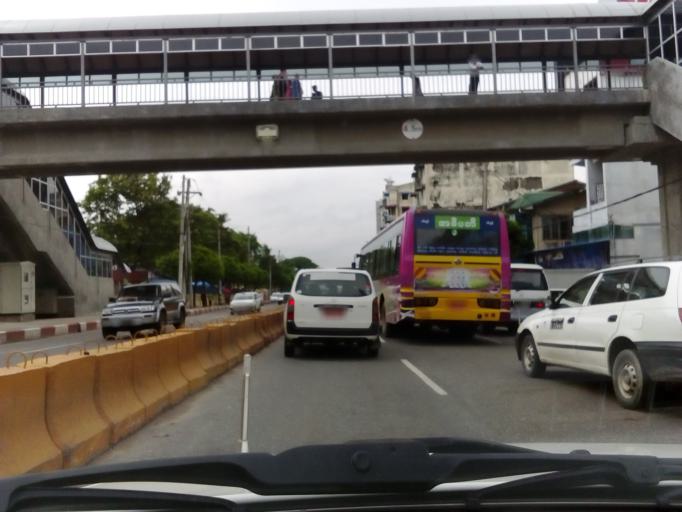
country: MM
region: Yangon
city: Yangon
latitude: 16.8560
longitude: 96.1568
